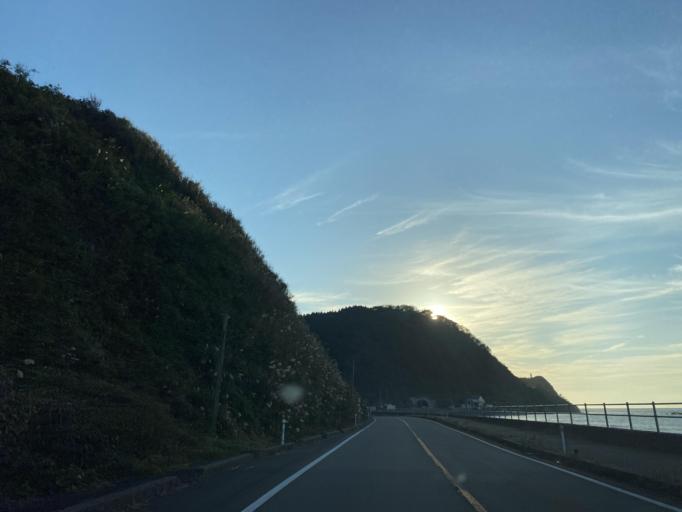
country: JP
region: Niigata
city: Kashiwazaki
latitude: 37.4866
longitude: 138.6297
